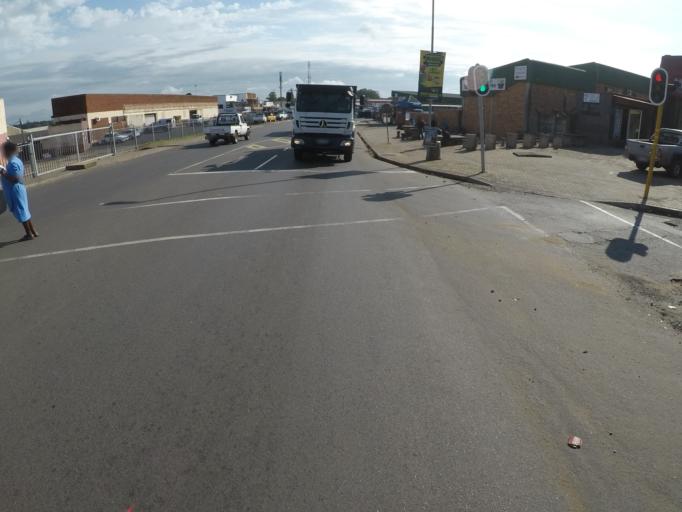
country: ZA
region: KwaZulu-Natal
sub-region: uThungulu District Municipality
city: Empangeni
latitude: -28.7724
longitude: 31.9036
